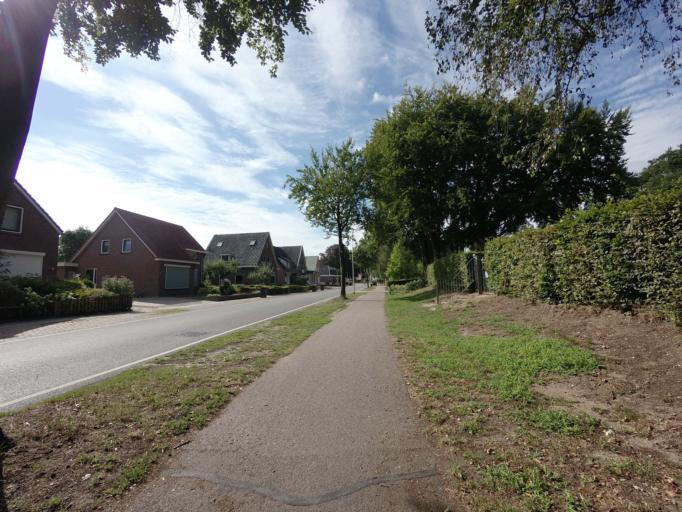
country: NL
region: Gelderland
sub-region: Gemeente Lochem
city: Harfsen
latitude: 52.2780
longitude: 6.2721
